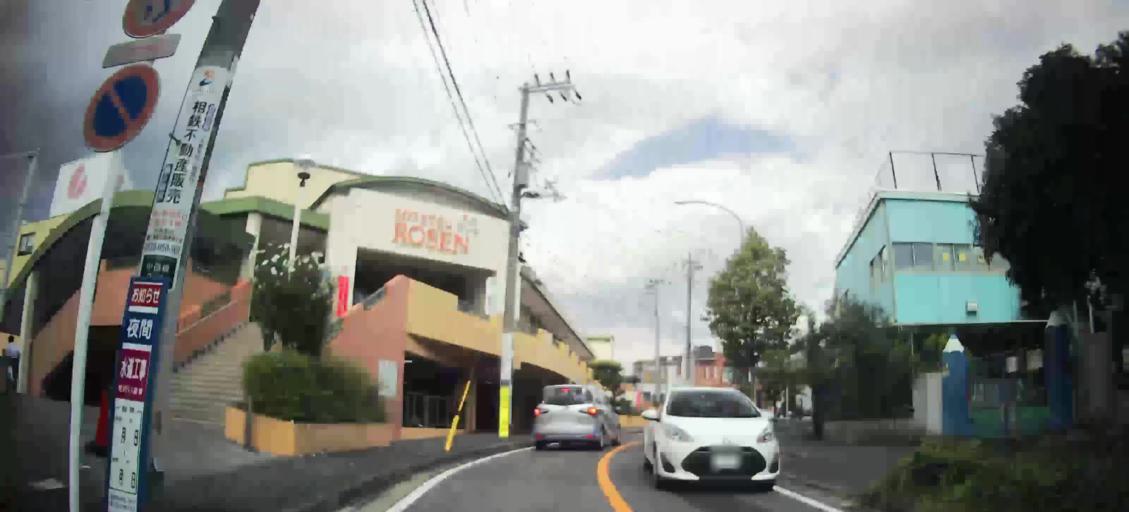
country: JP
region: Kanagawa
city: Minami-rinkan
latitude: 35.4878
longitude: 139.5433
